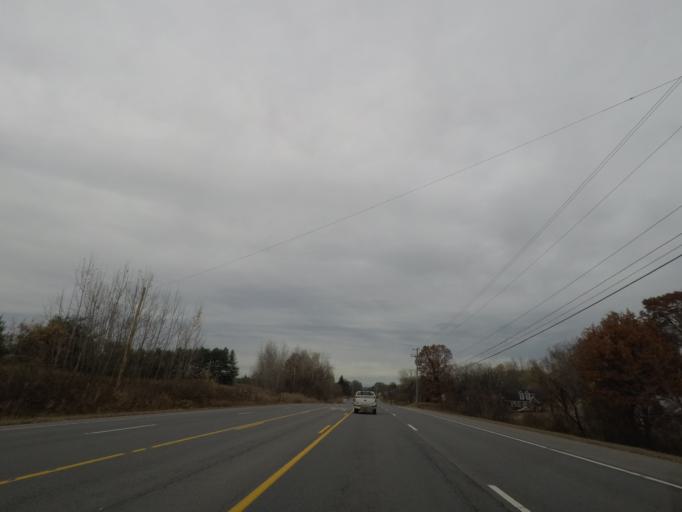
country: US
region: New York
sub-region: Saratoga County
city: Country Knolls
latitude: 42.8887
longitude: -73.7728
